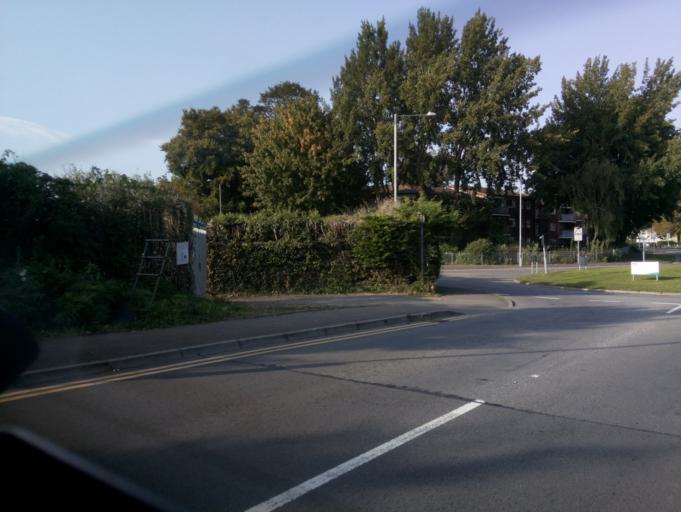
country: GB
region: Wales
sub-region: Torfaen County Borough
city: Cwmbran
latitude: 51.6588
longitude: -3.0130
